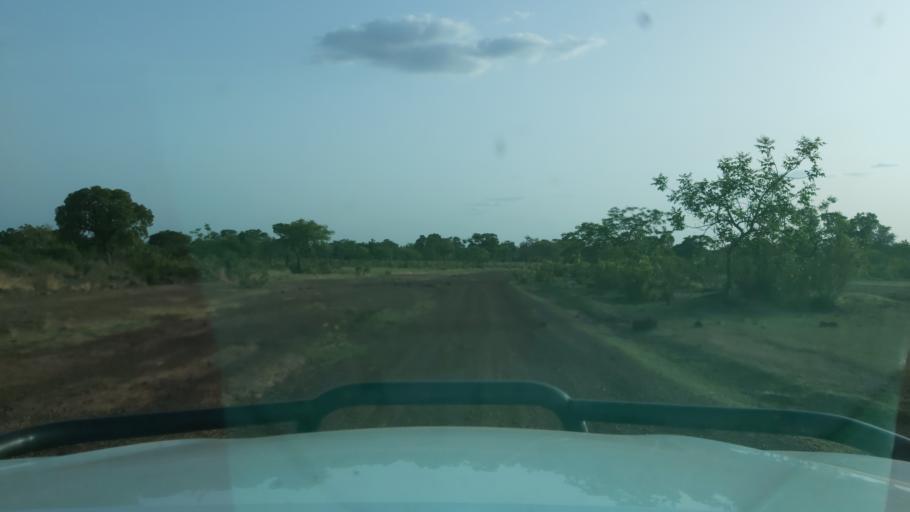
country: ML
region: Koulikoro
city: Kolokani
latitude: 13.2072
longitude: -7.9139
